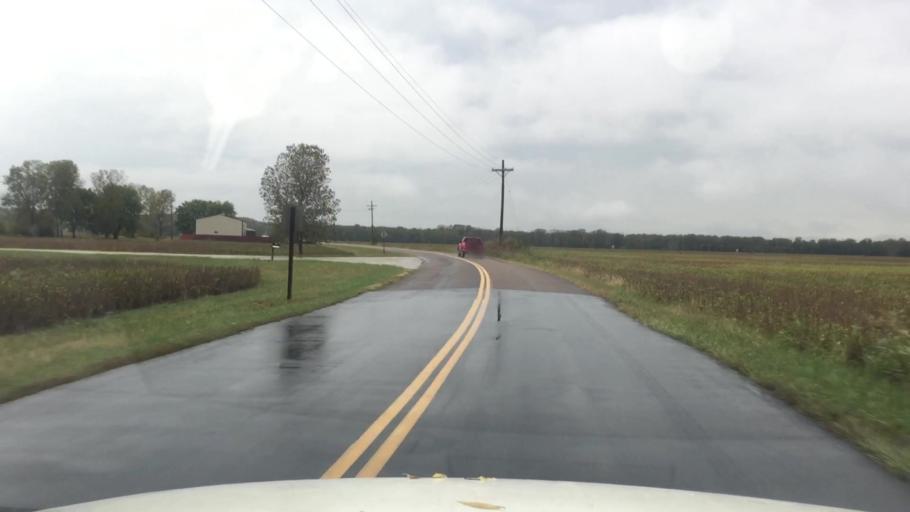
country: US
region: Missouri
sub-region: Boone County
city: Columbia
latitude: 38.8867
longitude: -92.4535
